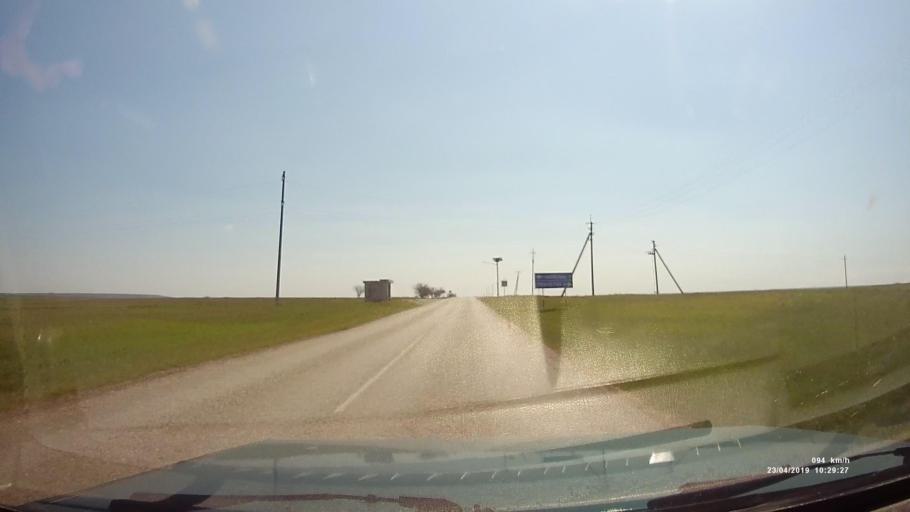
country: RU
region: Kalmykiya
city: Yashalta
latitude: 46.5984
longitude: 42.5268
